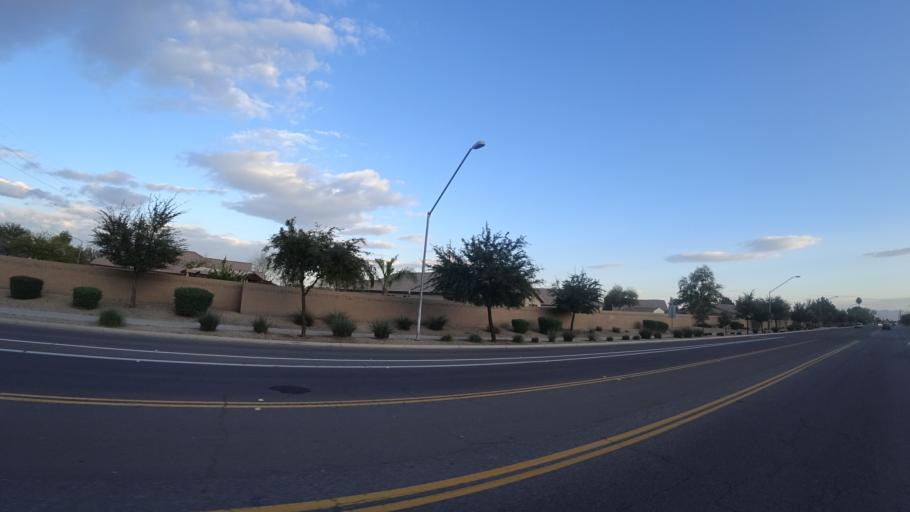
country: US
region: Arizona
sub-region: Maricopa County
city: Peoria
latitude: 33.5446
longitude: -112.2378
